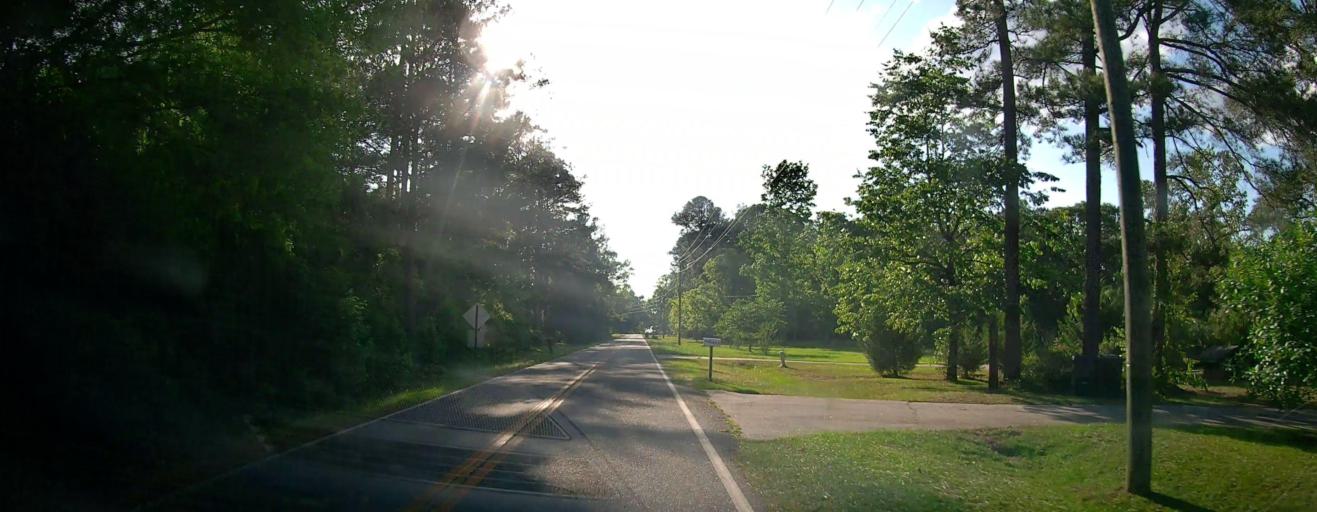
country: US
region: Georgia
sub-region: Peach County
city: Byron
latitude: 32.6715
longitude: -83.7932
